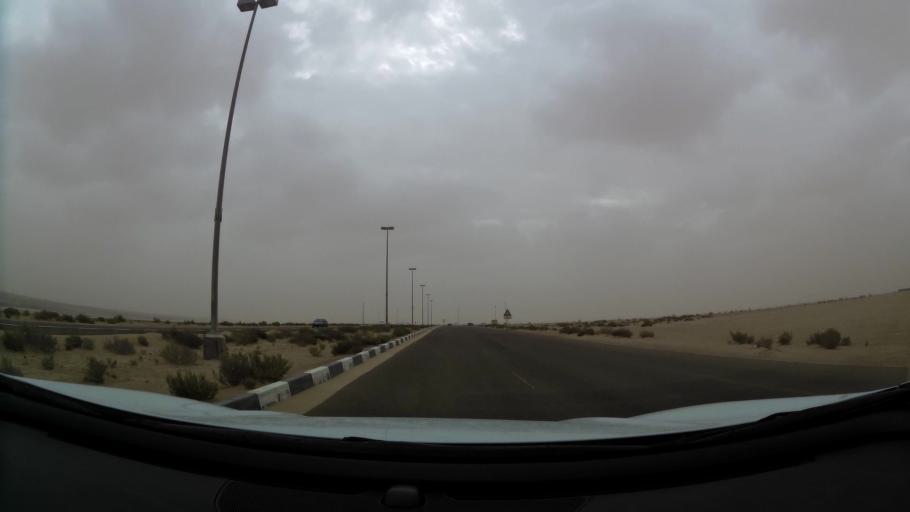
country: AE
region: Abu Dhabi
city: Abu Dhabi
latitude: 24.4623
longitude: 54.6869
